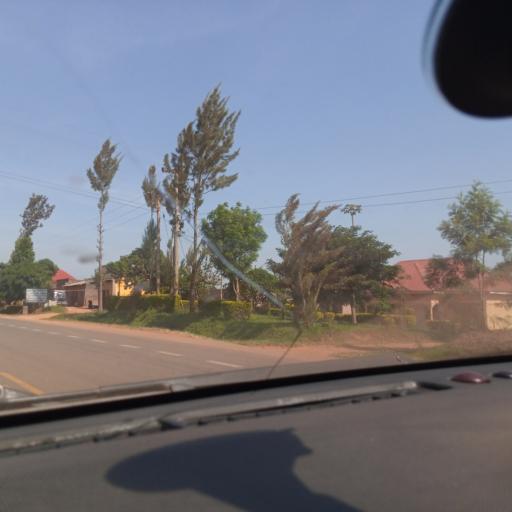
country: UG
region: Central Region
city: Masaka
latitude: -0.3255
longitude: 31.7316
